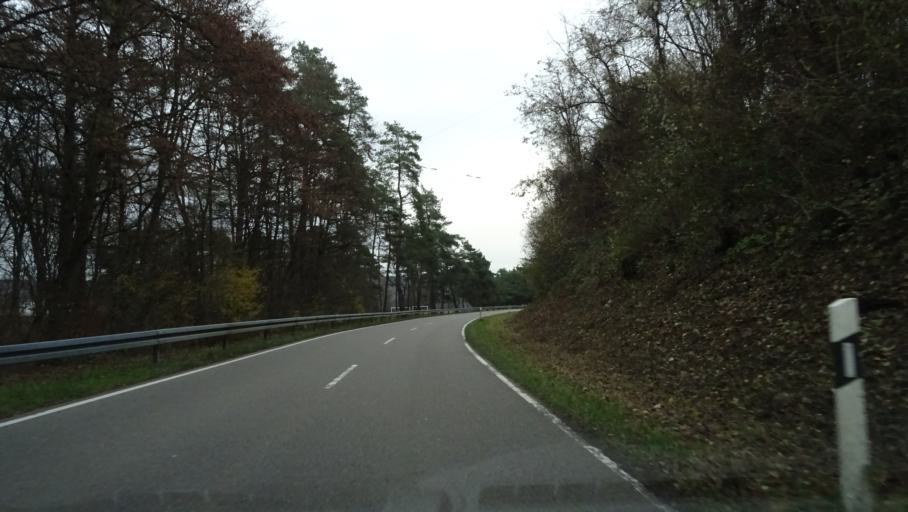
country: DE
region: Baden-Wuerttemberg
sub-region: Karlsruhe Region
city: Binau
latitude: 49.3606
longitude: 9.0721
